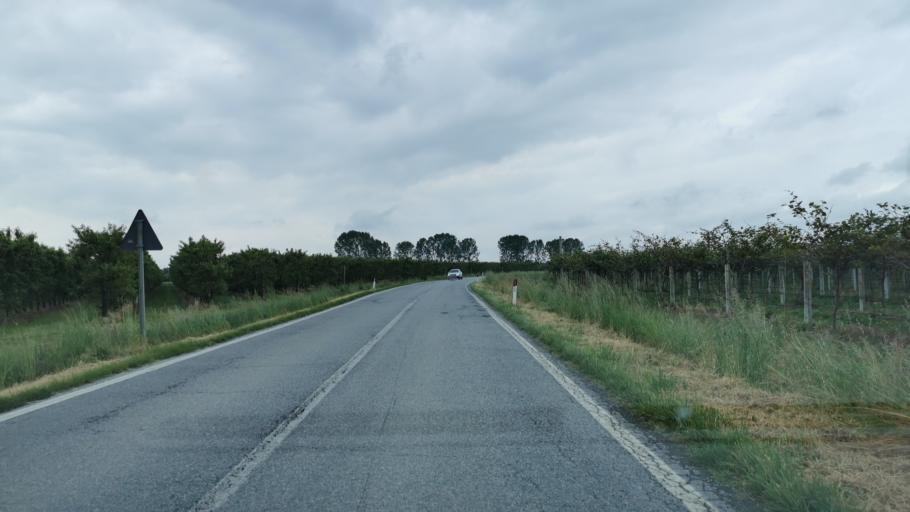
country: IT
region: Piedmont
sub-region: Provincia di Cuneo
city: Lagnasco
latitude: 44.6001
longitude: 7.5694
